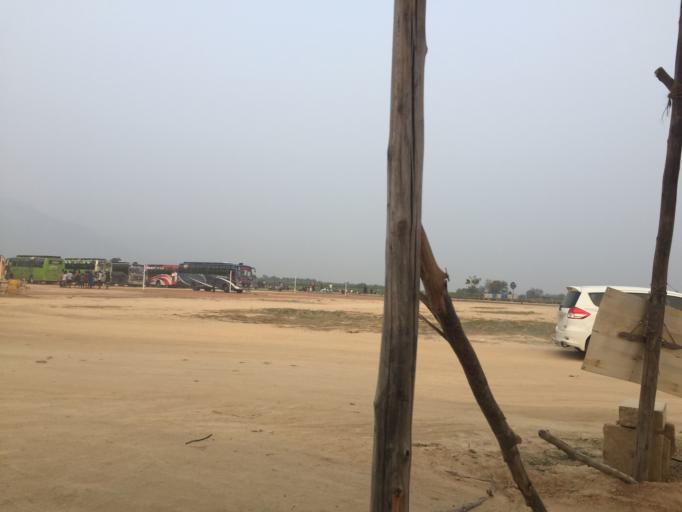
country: IN
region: Tamil Nadu
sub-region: Coimbatore
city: Perur
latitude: 10.9684
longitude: 76.7396
